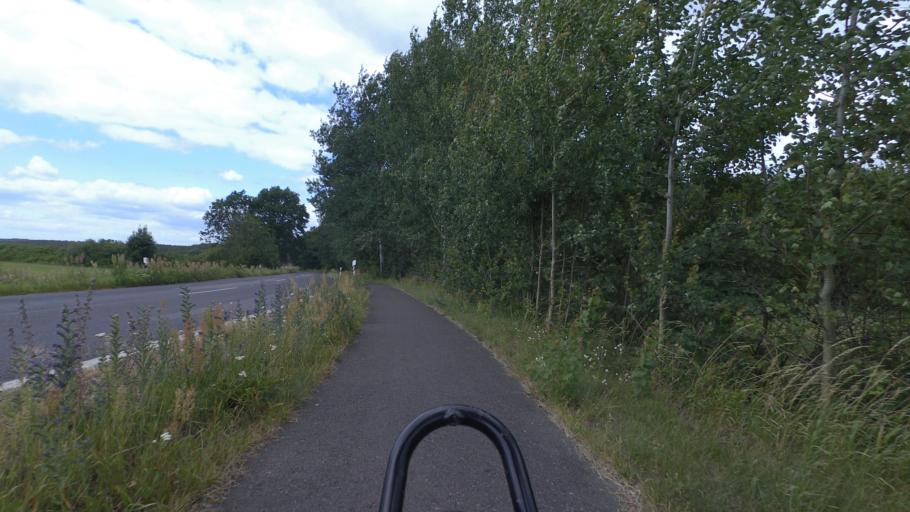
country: DE
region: Brandenburg
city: Trebbin
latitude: 52.2314
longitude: 13.1955
